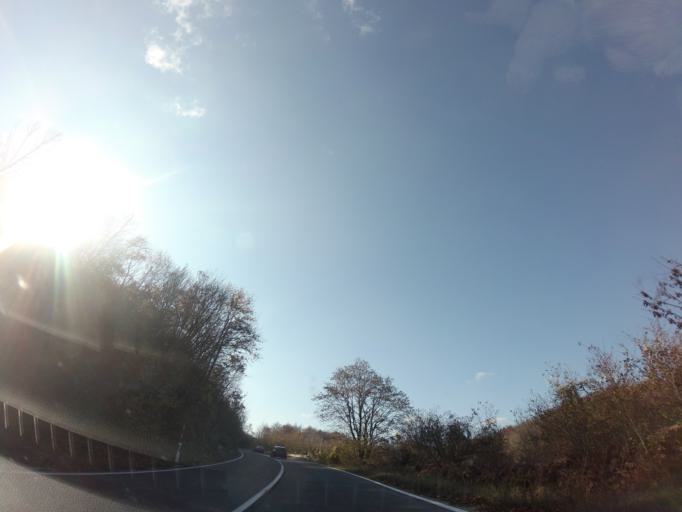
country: HR
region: Licko-Senjska
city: Jezerce
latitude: 44.9199
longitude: 15.6118
